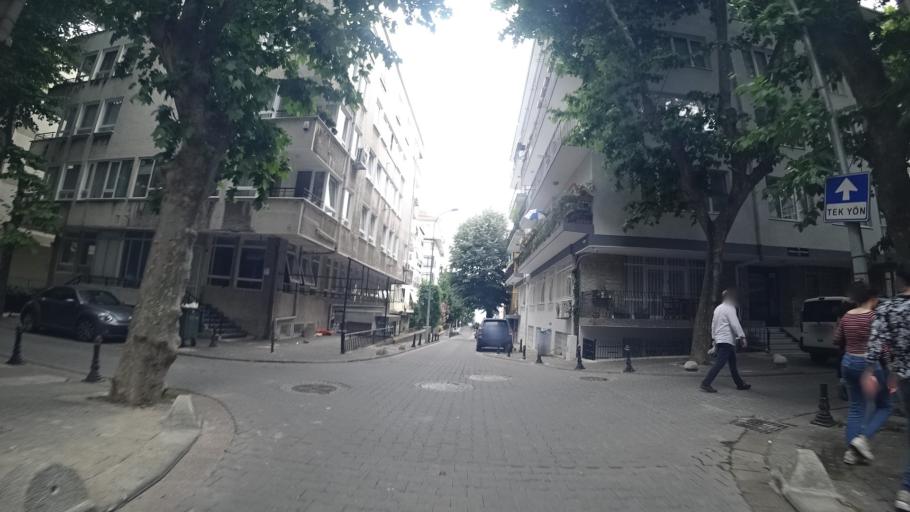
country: TR
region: Istanbul
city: UEskuedar
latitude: 40.9802
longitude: 29.0227
